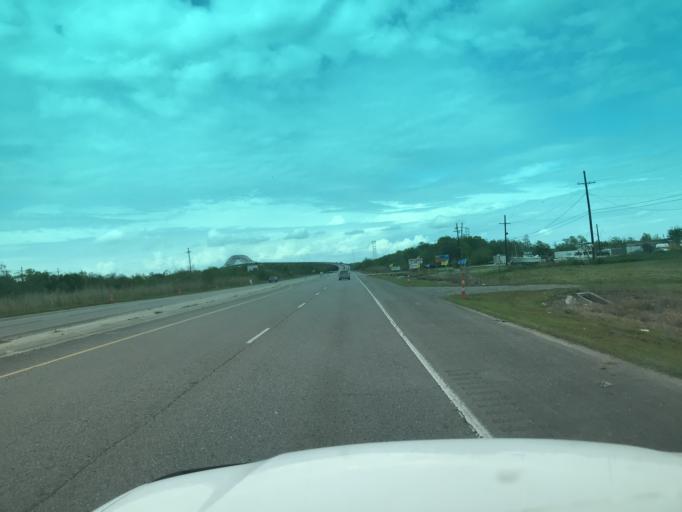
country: US
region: Louisiana
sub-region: Saint Bernard Parish
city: Chalmette
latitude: 29.9897
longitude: -89.9433
